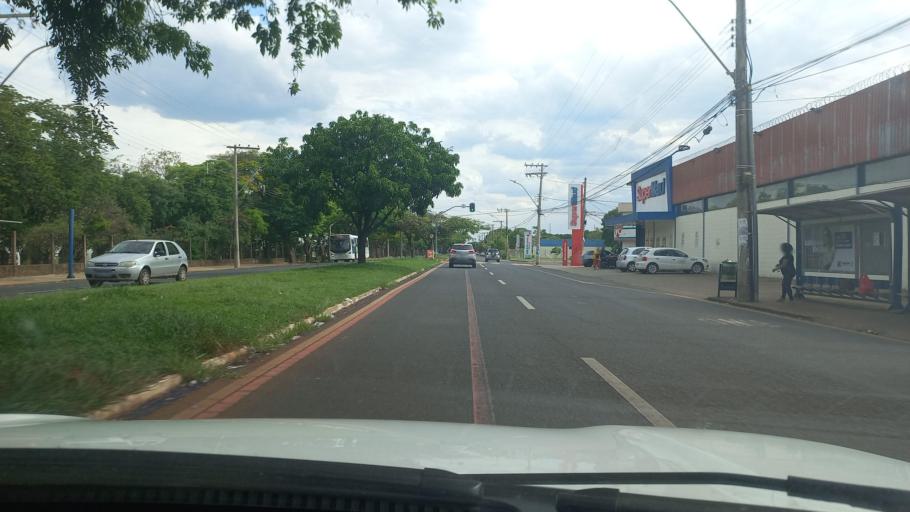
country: BR
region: Minas Gerais
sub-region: Uberaba
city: Uberaba
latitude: -19.7553
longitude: -47.9649
